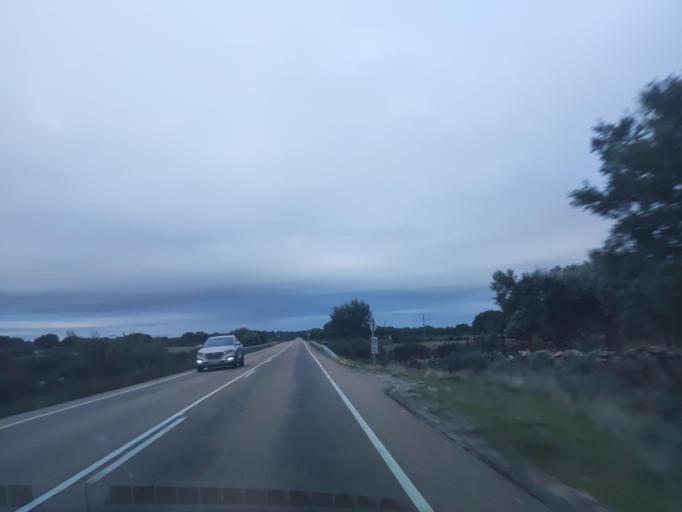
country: ES
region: Castille and Leon
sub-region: Provincia de Salamanca
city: Lumbrales
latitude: 40.9435
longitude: -6.7571
